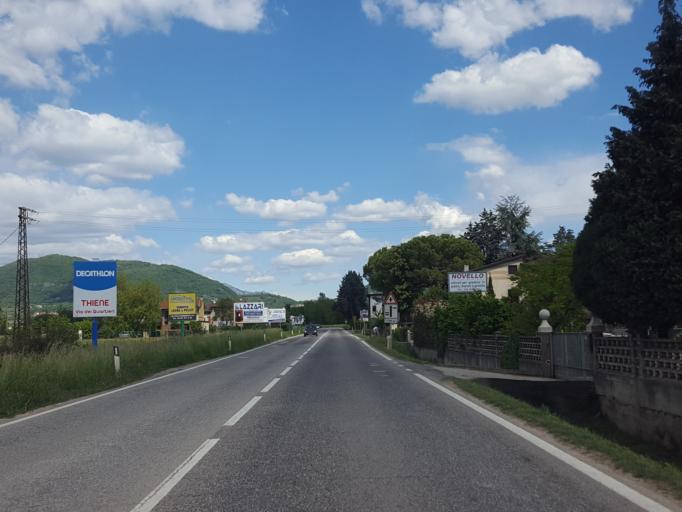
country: IT
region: Veneto
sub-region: Provincia di Vicenza
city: Castelgomberto
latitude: 45.5752
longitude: 11.3834
